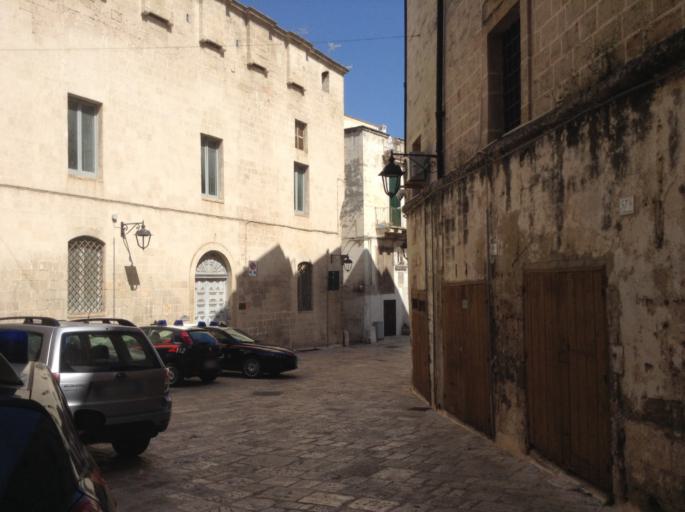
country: IT
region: Apulia
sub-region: Provincia di Bari
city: Monopoli
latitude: 40.9517
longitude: 17.3021
